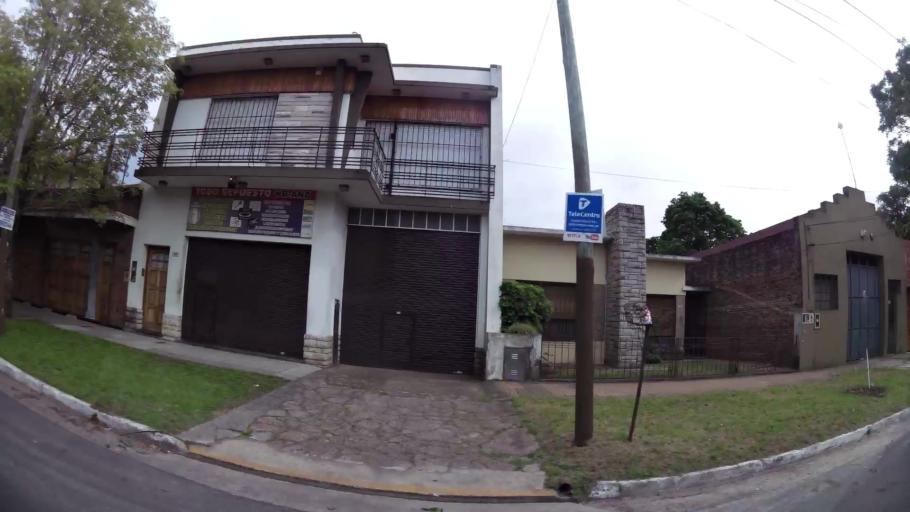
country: AR
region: Buenos Aires
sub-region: Partido de Quilmes
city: Quilmes
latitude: -34.7369
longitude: -58.2700
